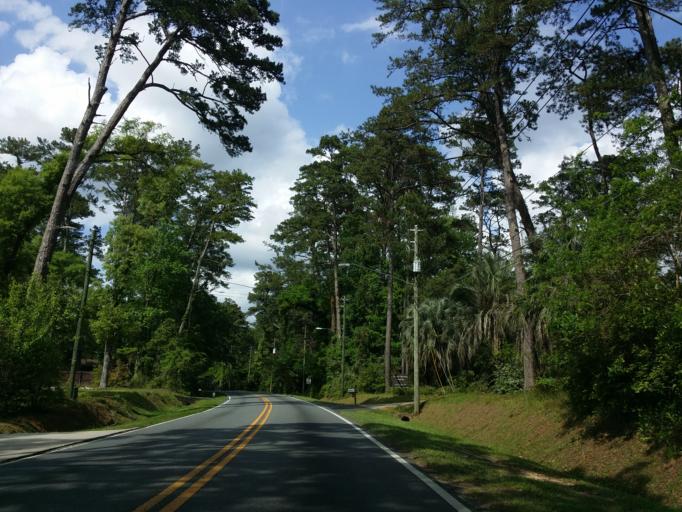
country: US
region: Florida
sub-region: Leon County
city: Tallahassee
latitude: 30.4227
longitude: -84.2625
